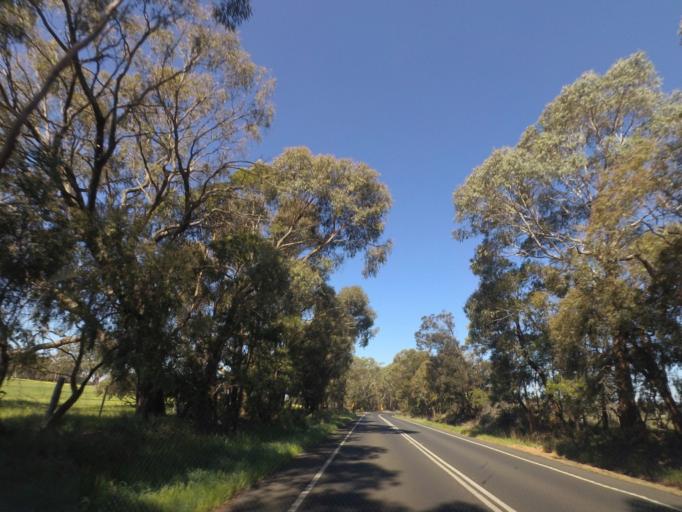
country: AU
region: Victoria
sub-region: Whittlesea
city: Whittlesea
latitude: -37.3279
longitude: 144.9805
